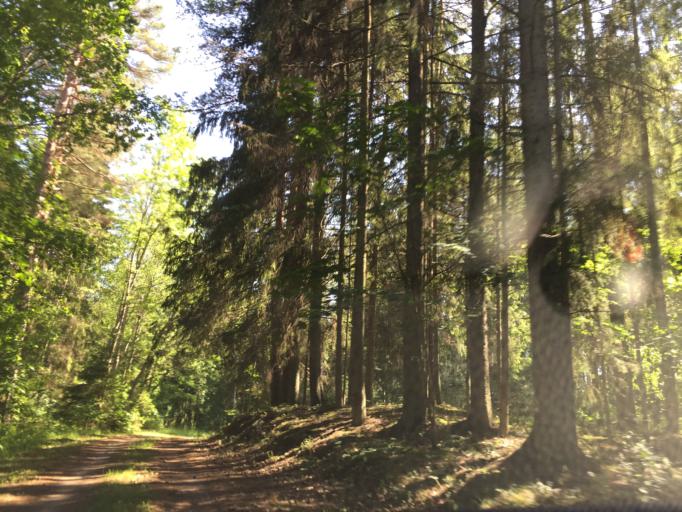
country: LV
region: Tukuma Rajons
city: Tukums
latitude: 57.0208
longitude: 23.2414
